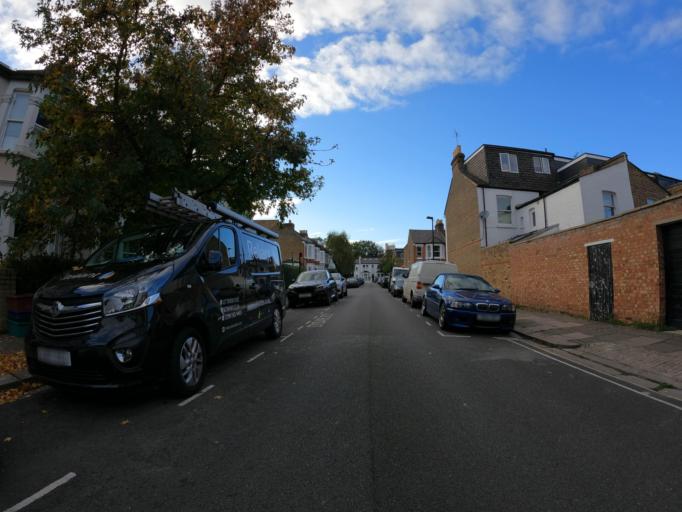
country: GB
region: England
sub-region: Greater London
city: Acton
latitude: 51.4867
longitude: -0.2748
